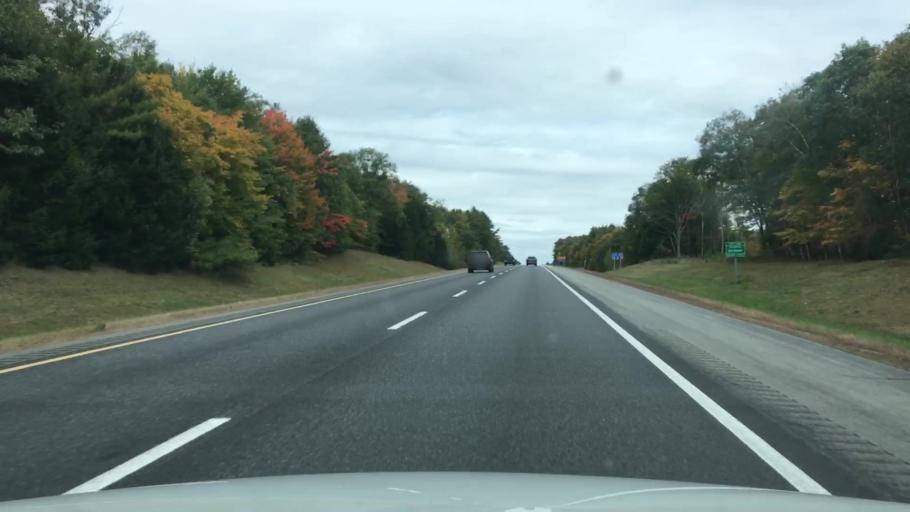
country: US
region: Maine
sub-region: Sagadahoc County
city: Richmond
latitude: 44.1639
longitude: -69.8346
